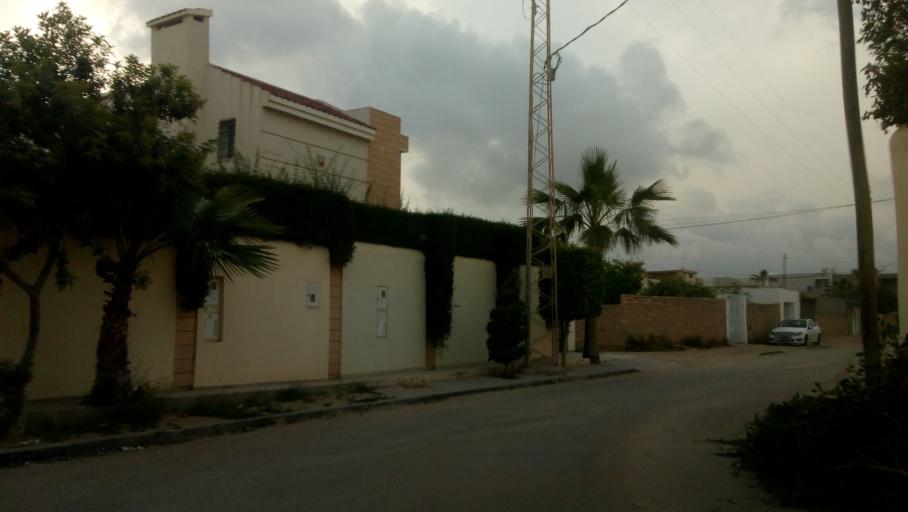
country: TN
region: Safaqis
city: Sfax
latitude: 34.7693
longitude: 10.7011
